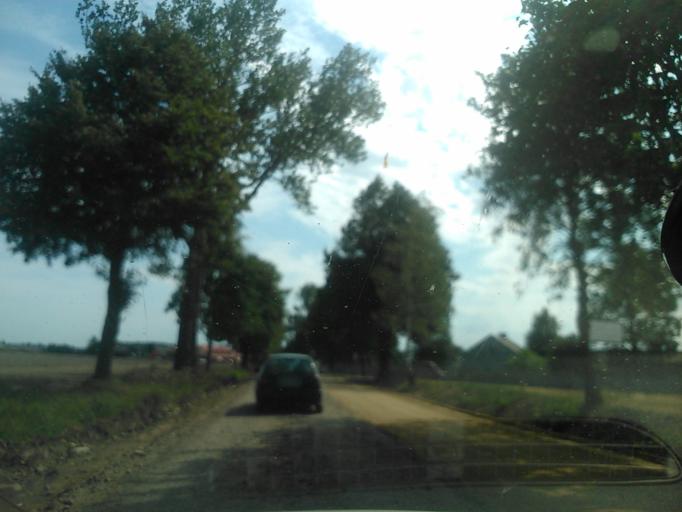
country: PL
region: Warmian-Masurian Voivodeship
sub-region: Powiat dzialdowski
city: Ilowo -Osada
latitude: 53.2022
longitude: 20.2432
